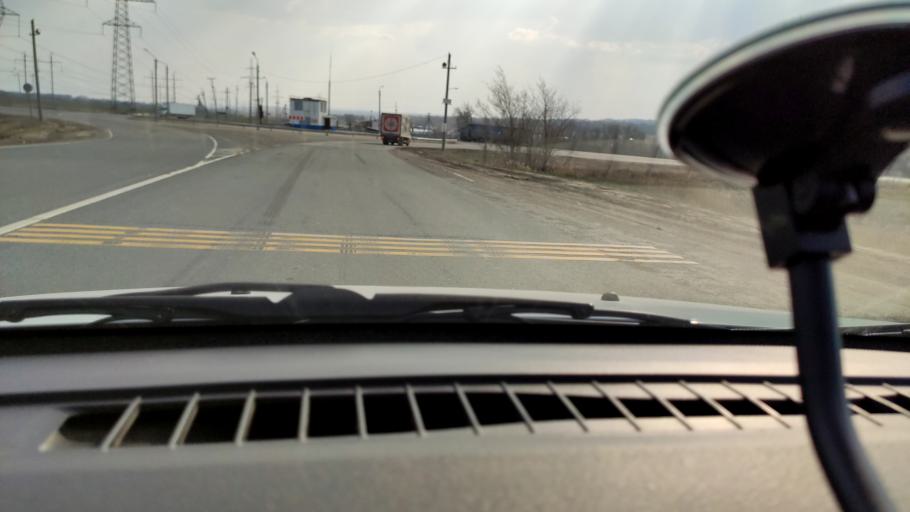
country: RU
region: Samara
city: Dubovyy Umet
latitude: 53.0637
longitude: 50.3770
